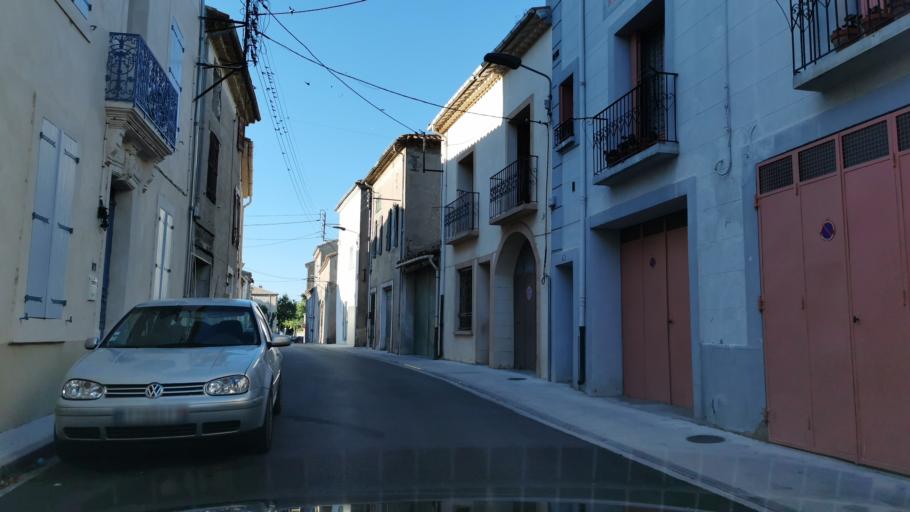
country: FR
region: Languedoc-Roussillon
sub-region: Departement de l'Aude
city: Moussan
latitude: 43.2430
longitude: 2.9972
